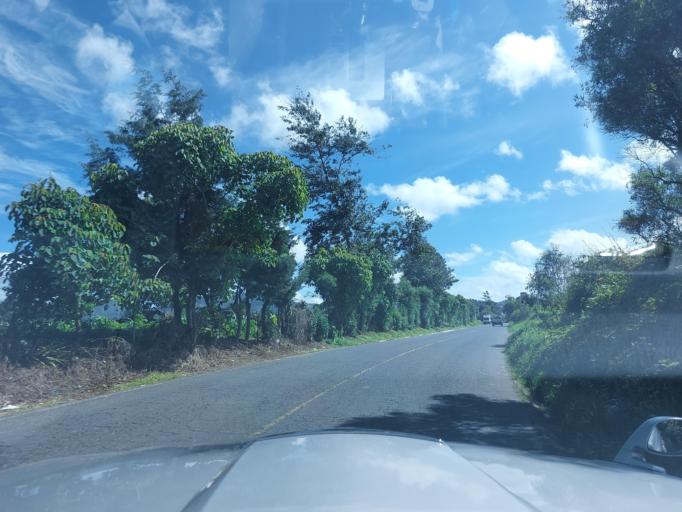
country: GT
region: Chimaltenango
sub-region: Municipio de San Juan Comalapa
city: Comalapa
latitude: 14.7214
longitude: -90.8892
